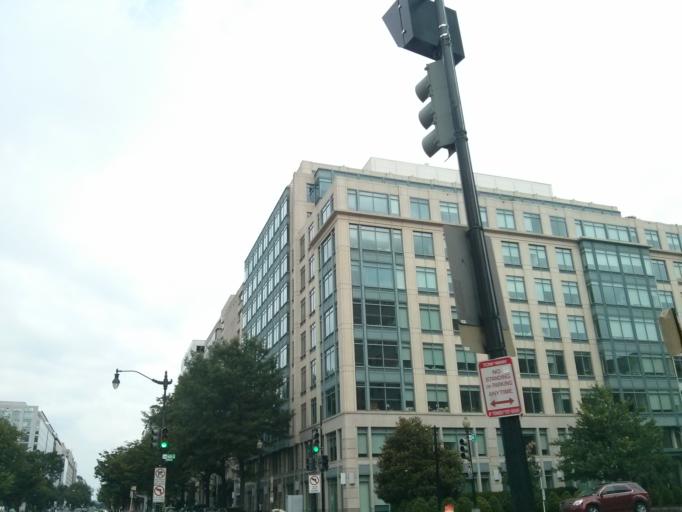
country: US
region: Washington, D.C.
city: Washington, D.C.
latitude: 38.9026
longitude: -77.0363
